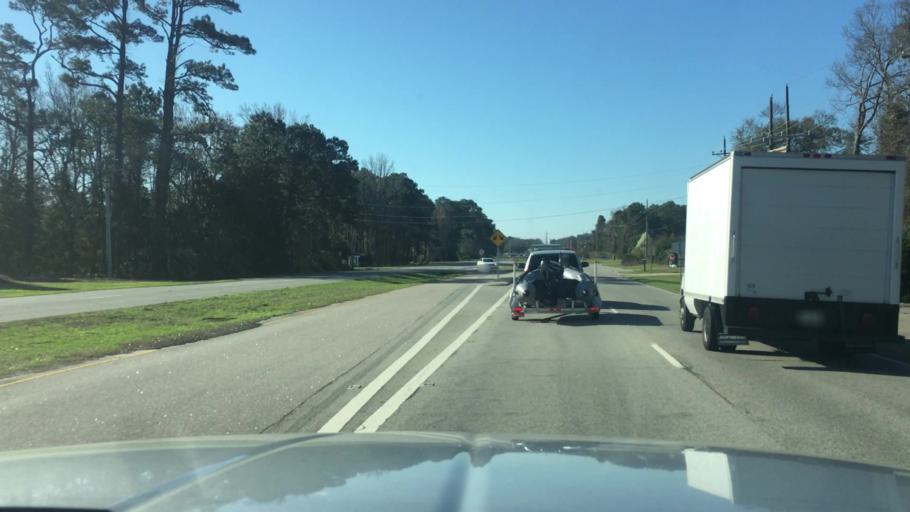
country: US
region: North Carolina
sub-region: New Hanover County
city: Sea Breeze
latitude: 34.0704
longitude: -77.8966
